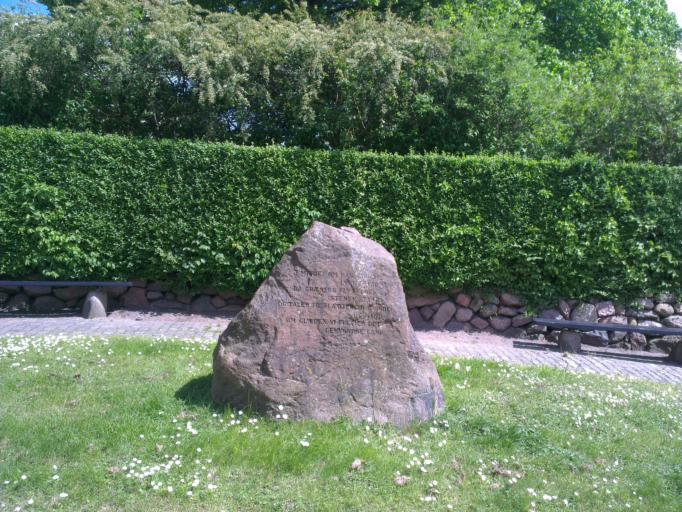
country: DK
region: Capital Region
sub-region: Hillerod Kommune
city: Hillerod
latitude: 55.9291
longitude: 12.3045
